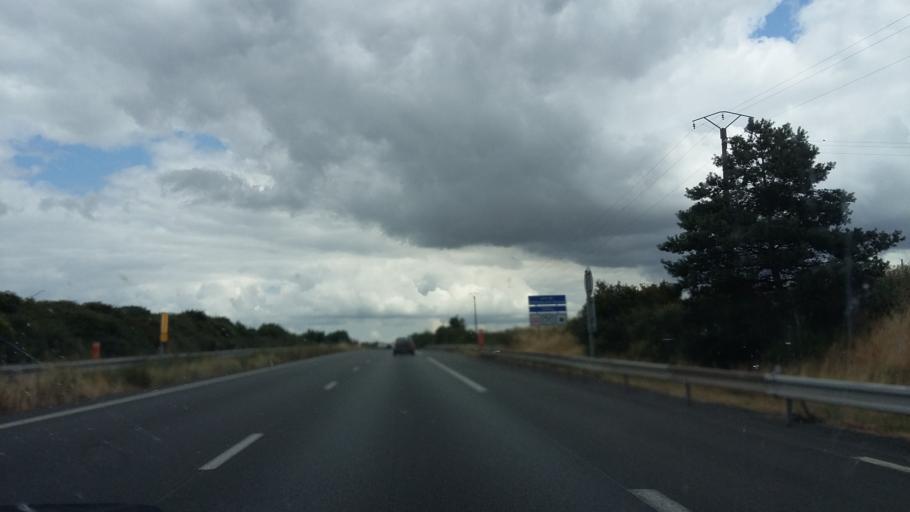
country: FR
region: Poitou-Charentes
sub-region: Departement de la Vienne
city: Antran
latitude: 46.8934
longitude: 0.5195
